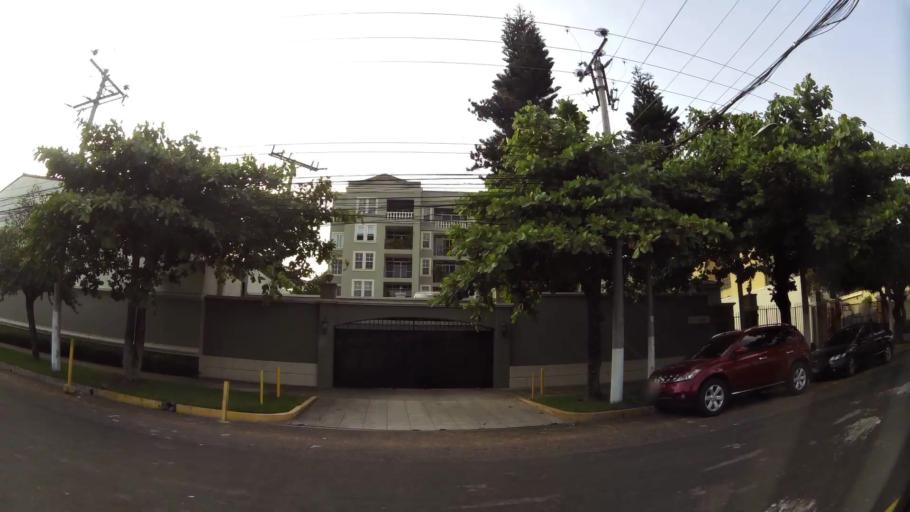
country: SV
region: La Libertad
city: Antiguo Cuscatlan
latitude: 13.6934
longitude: -89.2439
